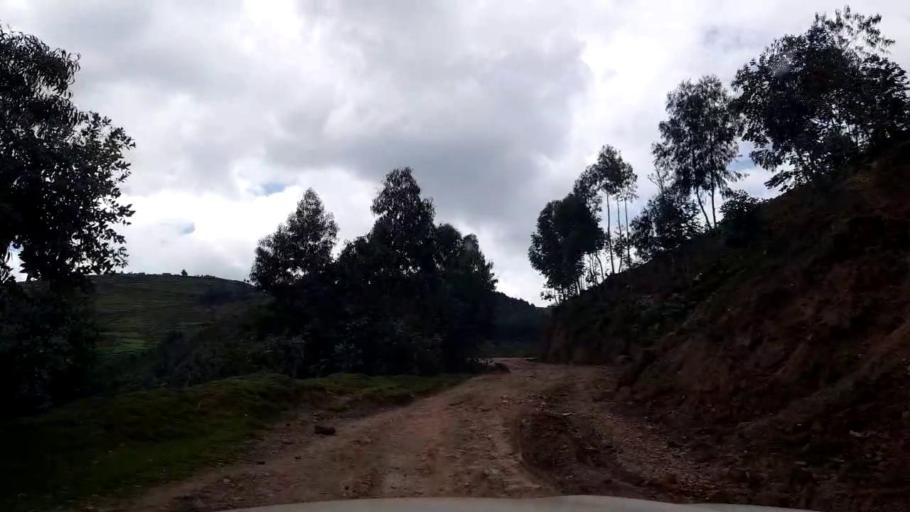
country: RW
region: Western Province
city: Kibuye
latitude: -1.9011
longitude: 29.4542
